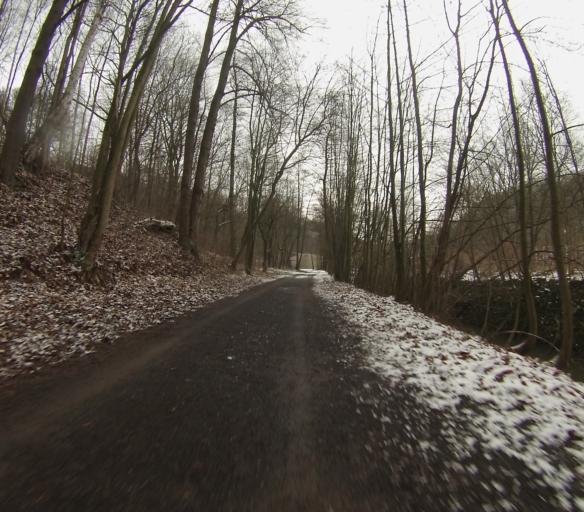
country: CZ
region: Ustecky
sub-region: Okres Decin
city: Decin
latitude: 50.7596
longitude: 14.2558
